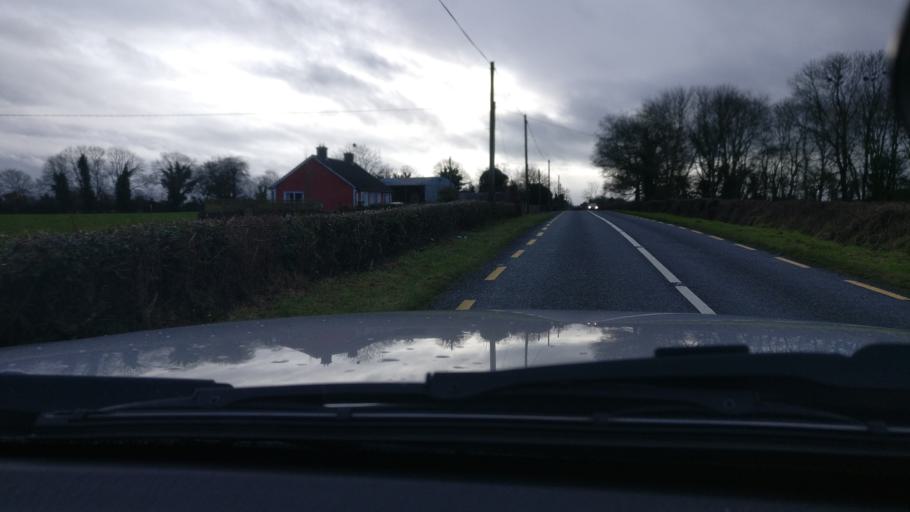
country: IE
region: Leinster
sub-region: An Iarmhi
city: Moate
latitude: 53.6007
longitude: -7.7136
